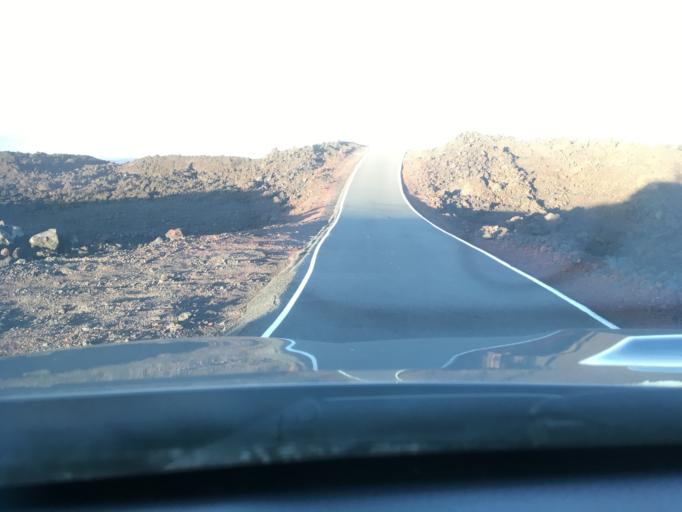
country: US
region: Hawaii
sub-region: Hawaii County
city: Honaunau-Napoopoo
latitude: 19.5381
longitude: -155.5750
